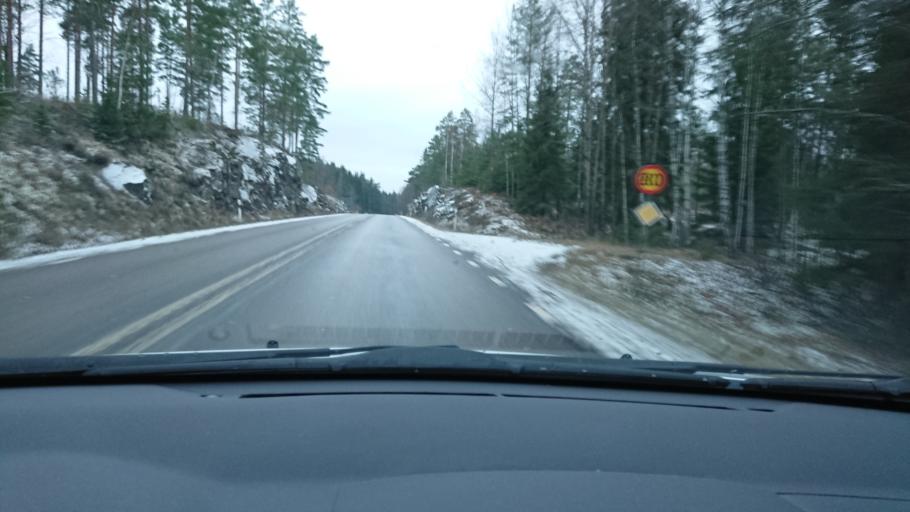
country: SE
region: Kalmar
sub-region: Hultsfreds Kommun
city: Hultsfred
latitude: 57.4908
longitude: 15.8247
